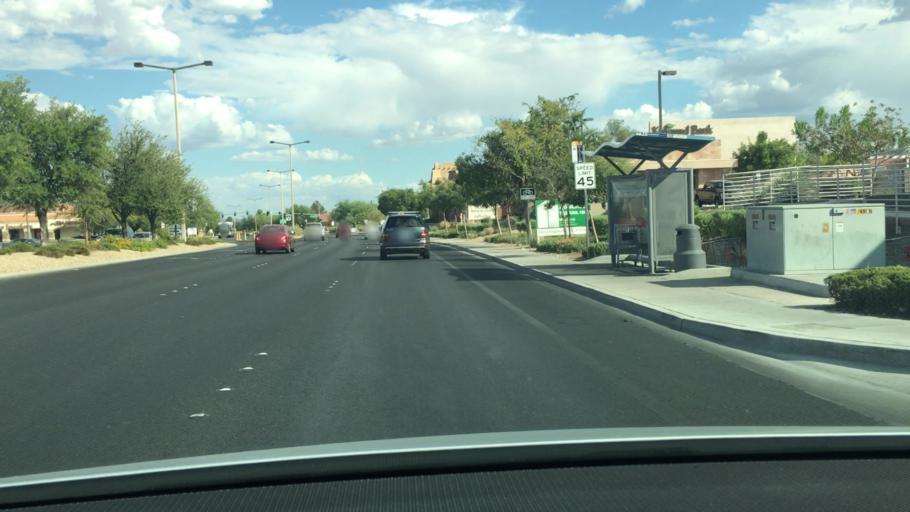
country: US
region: Nevada
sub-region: Clark County
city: Summerlin South
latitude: 36.1991
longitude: -115.2816
